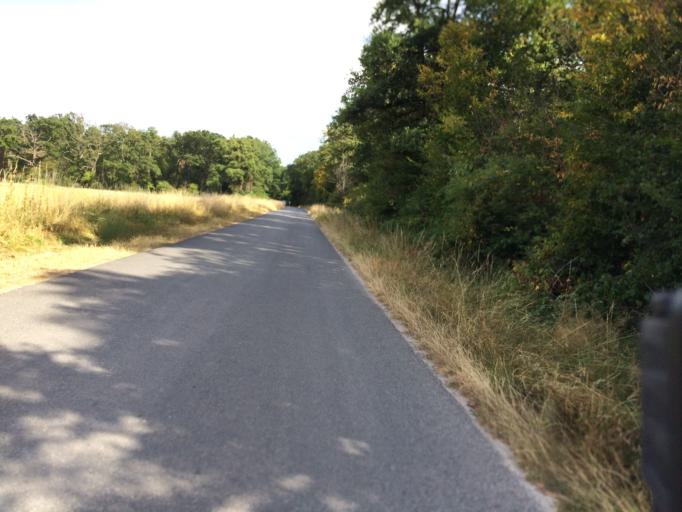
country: FR
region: Ile-de-France
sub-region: Departement de l'Essonne
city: Tigery
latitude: 48.6499
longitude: 2.4911
